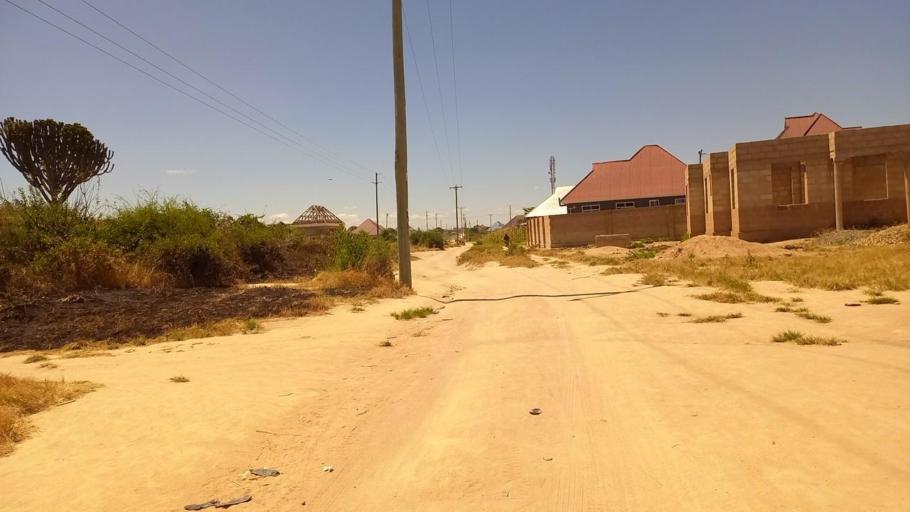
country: TZ
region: Dodoma
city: Dodoma
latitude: -6.1335
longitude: 35.7168
